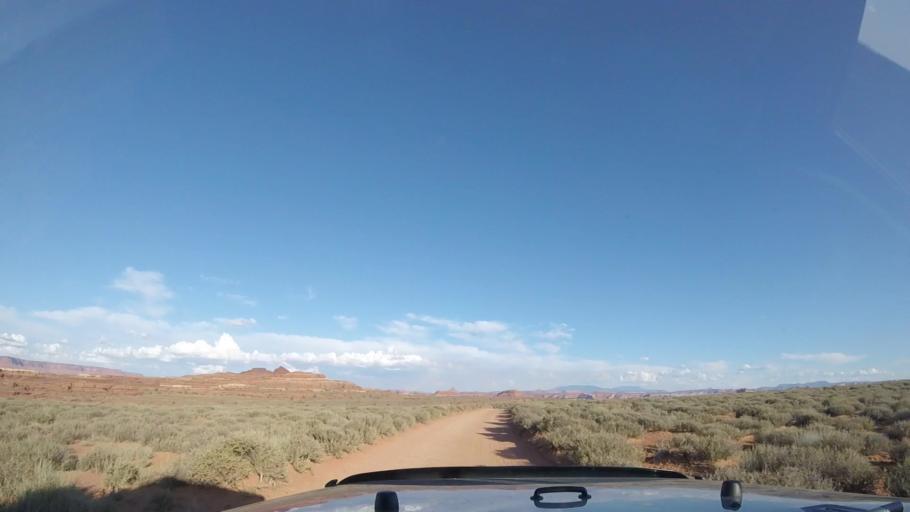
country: US
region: Utah
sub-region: Grand County
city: Moab
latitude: 38.2141
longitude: -109.7918
